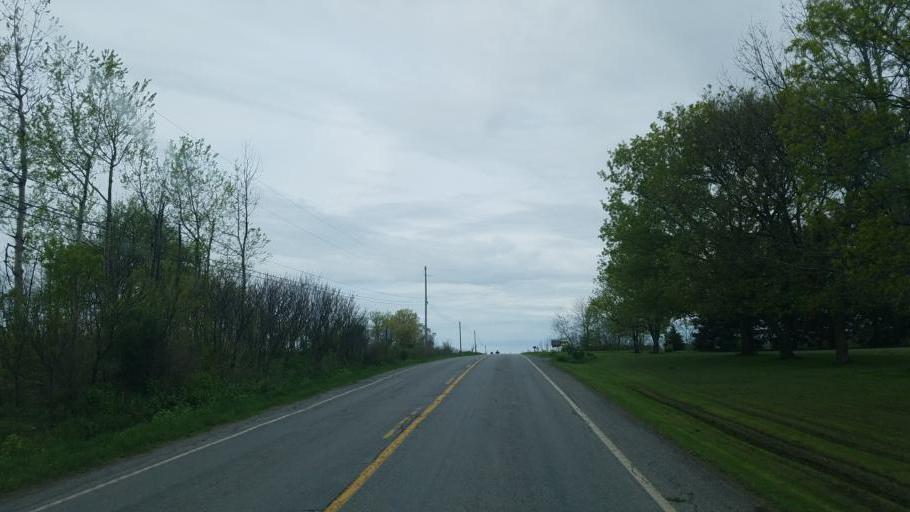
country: US
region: Pennsylvania
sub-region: Tioga County
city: Westfield
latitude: 41.9308
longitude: -77.7239
